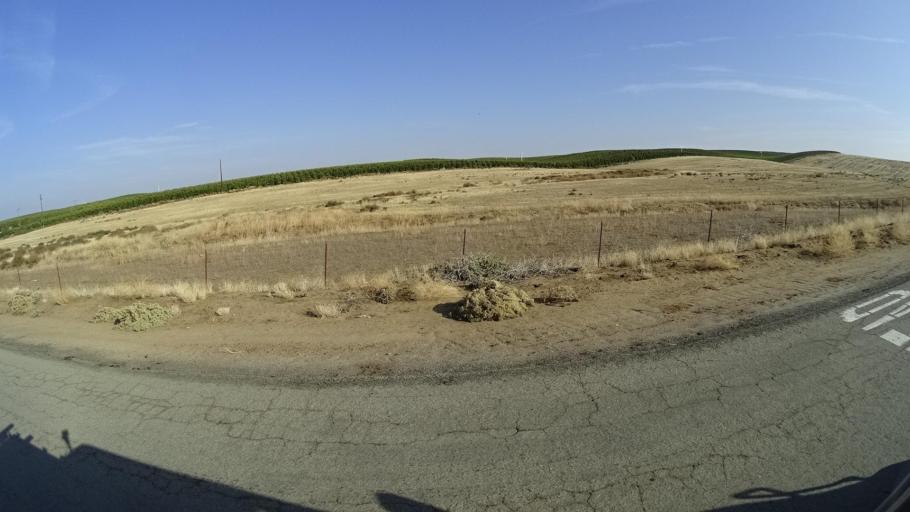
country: US
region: California
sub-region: Tulare County
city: Richgrove
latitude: 35.6587
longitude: -119.0753
